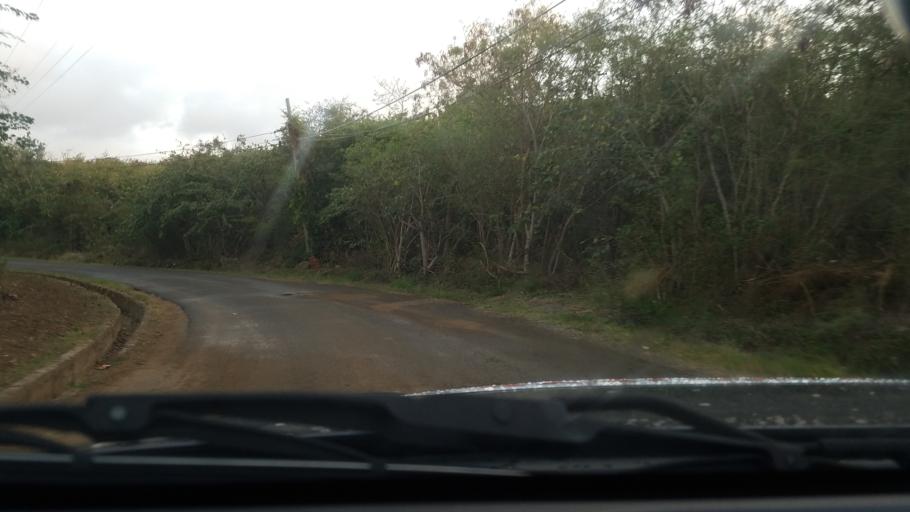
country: LC
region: Gros-Islet
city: Gros Islet
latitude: 14.0903
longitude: -60.9319
